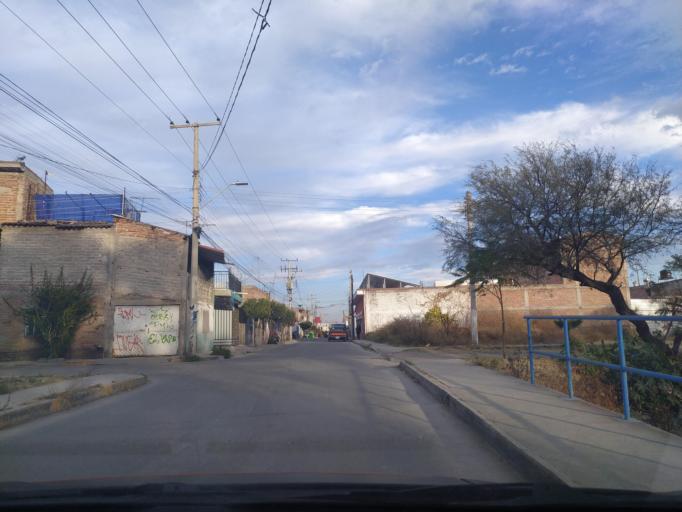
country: LA
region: Oudomxai
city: Muang La
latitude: 21.0327
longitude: 101.8824
